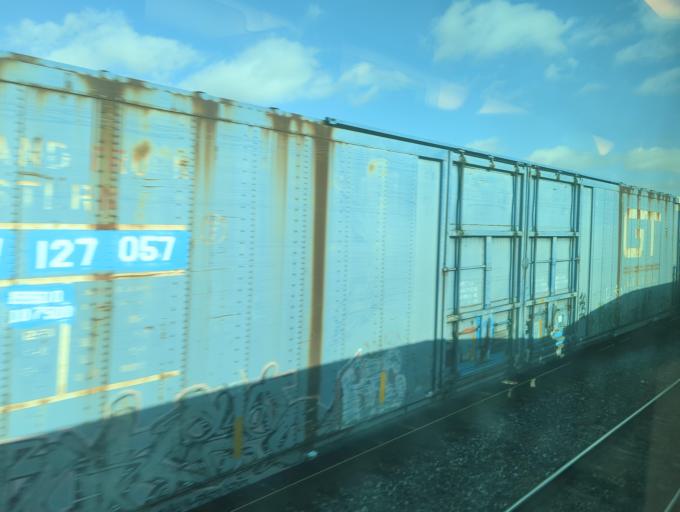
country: CA
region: Ontario
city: Burlington
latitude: 43.3187
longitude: -79.8457
